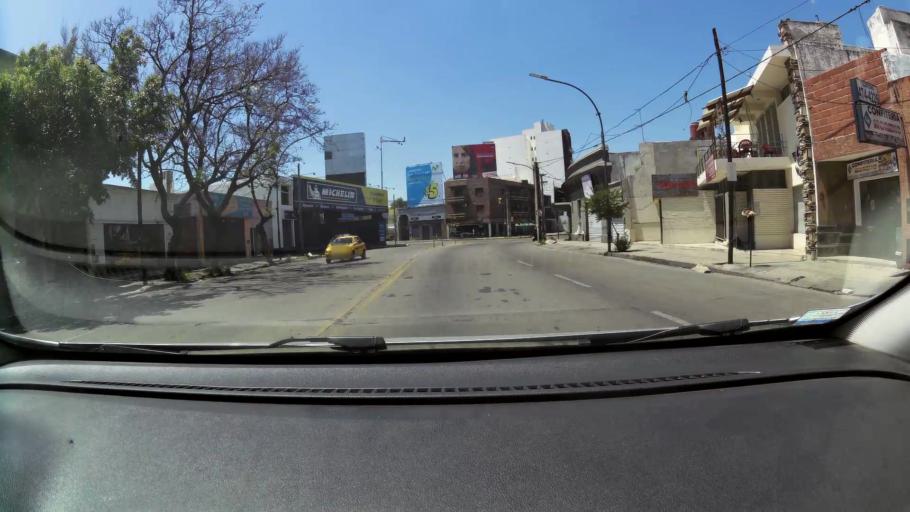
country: AR
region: Cordoba
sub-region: Departamento de Capital
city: Cordoba
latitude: -31.4010
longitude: -64.1974
